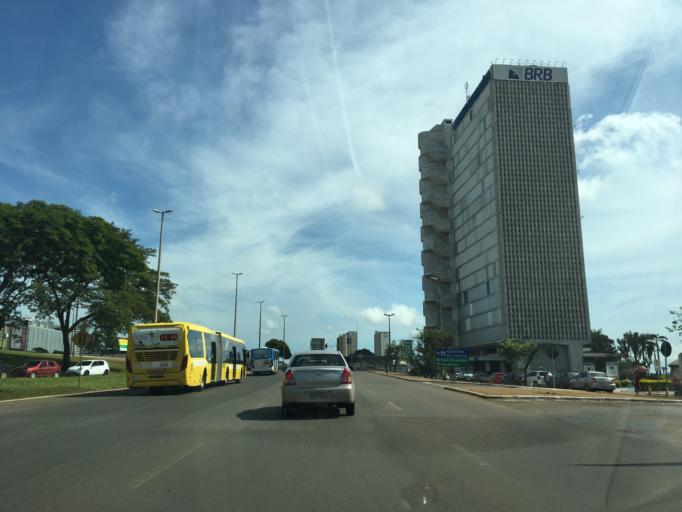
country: BR
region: Federal District
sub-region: Brasilia
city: Brasilia
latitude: -15.7989
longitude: -47.8839
